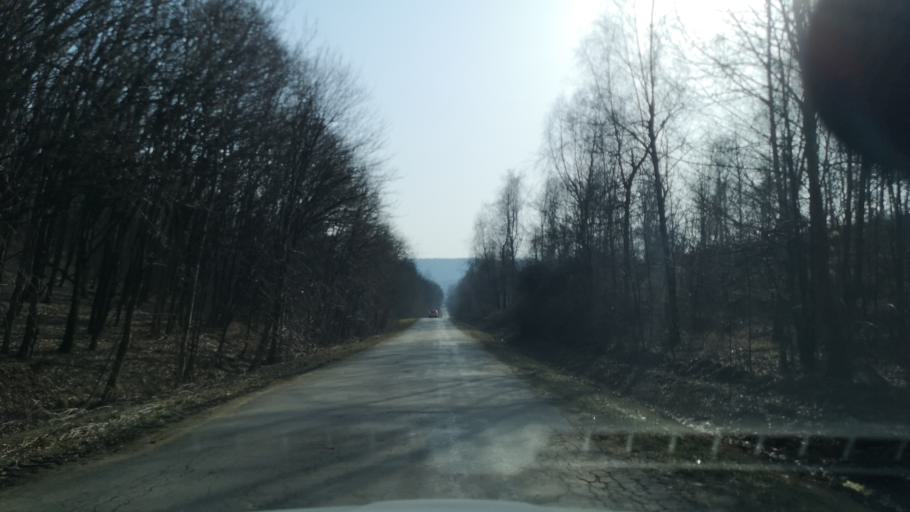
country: MD
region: Nisporeni
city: Nisporeni
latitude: 47.0984
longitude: 28.3153
